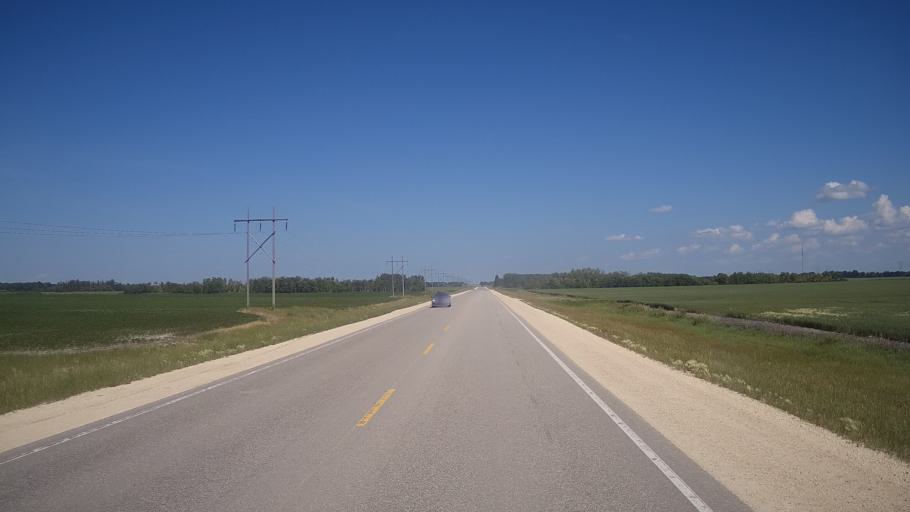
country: CA
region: Manitoba
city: Stonewall
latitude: 50.1227
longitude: -97.3752
